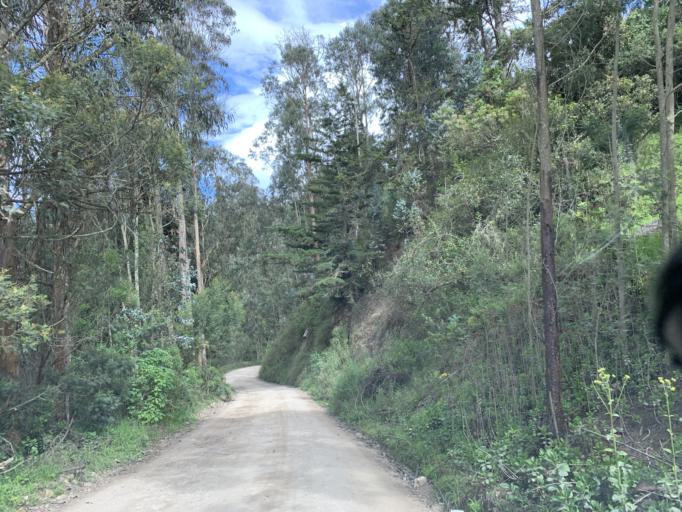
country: CO
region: Boyaca
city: Ramiriqui
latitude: 5.4126
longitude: -73.3284
